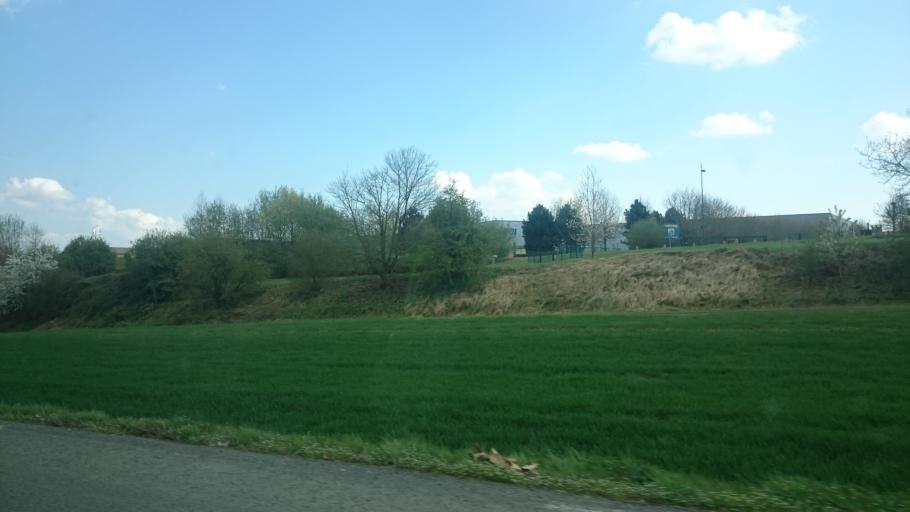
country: FR
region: Picardie
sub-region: Departement de l'Aisne
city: Harly
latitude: 49.8212
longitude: 3.2974
